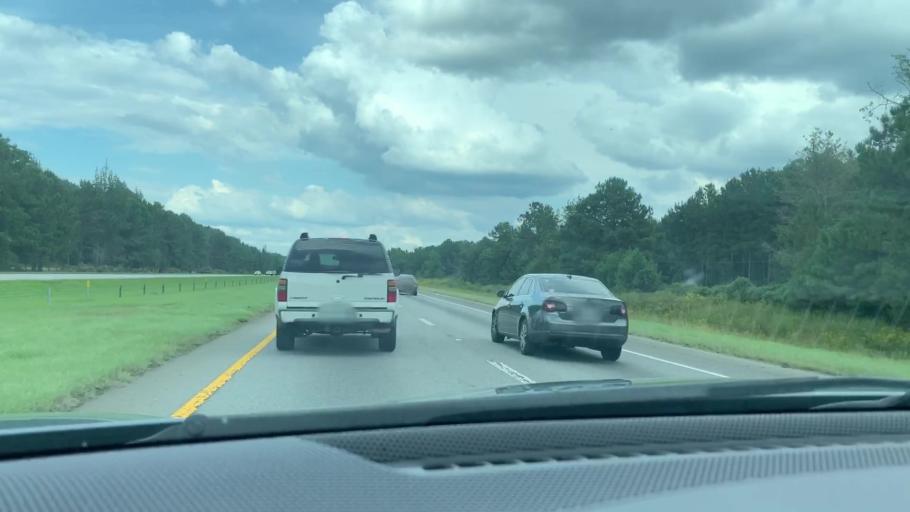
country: US
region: South Carolina
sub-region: Hampton County
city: Yemassee
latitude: 32.6087
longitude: -80.8961
